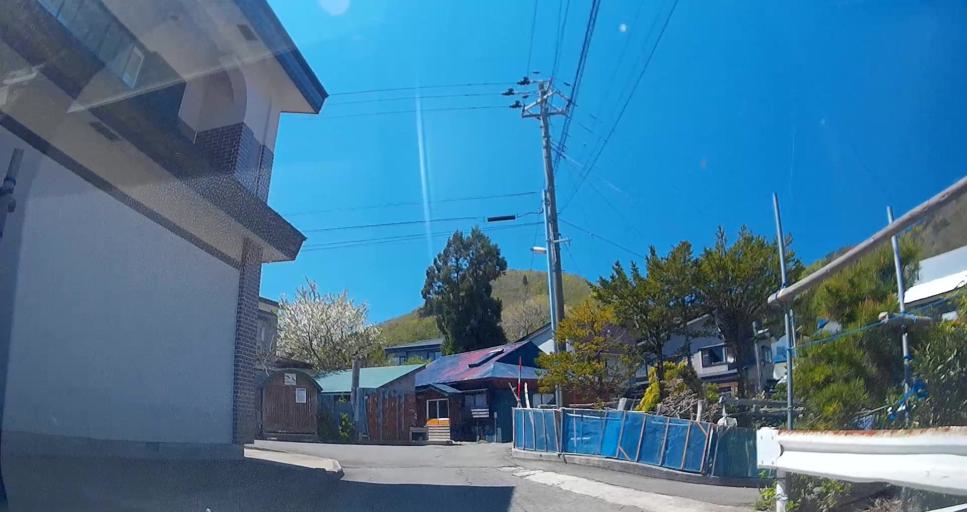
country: JP
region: Aomori
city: Mutsu
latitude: 41.3722
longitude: 141.4487
